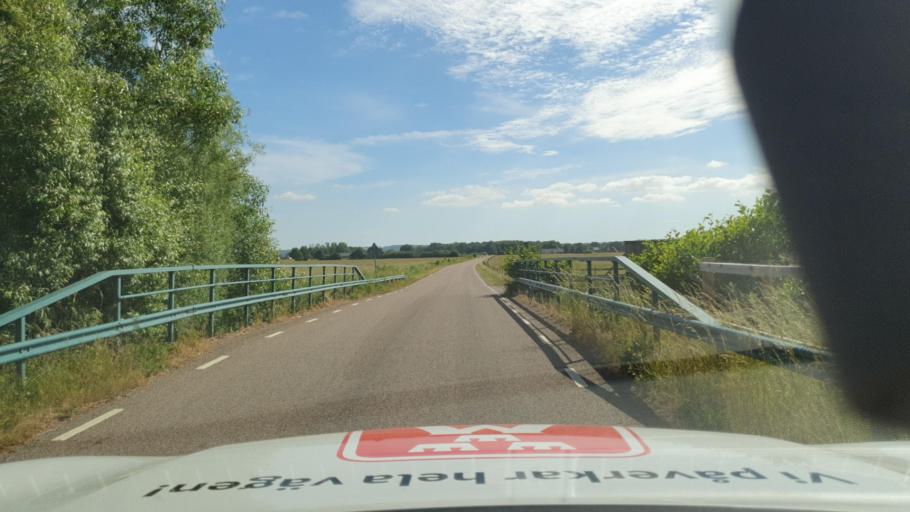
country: SE
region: Skane
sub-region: Sjobo Kommun
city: Blentarp
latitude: 55.6221
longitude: 13.6255
